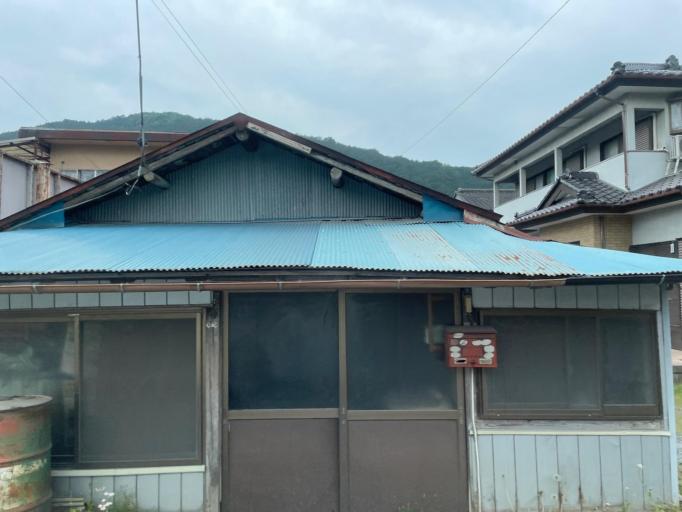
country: JP
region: Tochigi
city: Tochigi
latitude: 36.4416
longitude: 139.6522
